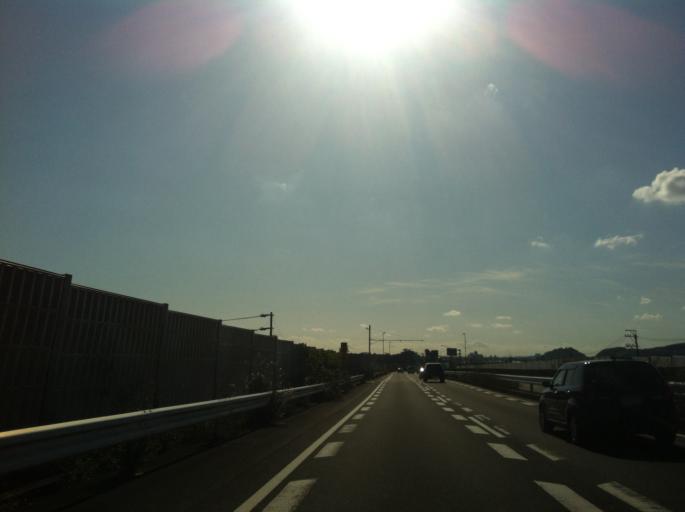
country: JP
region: Shizuoka
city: Fujieda
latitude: 34.9071
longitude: 138.2876
